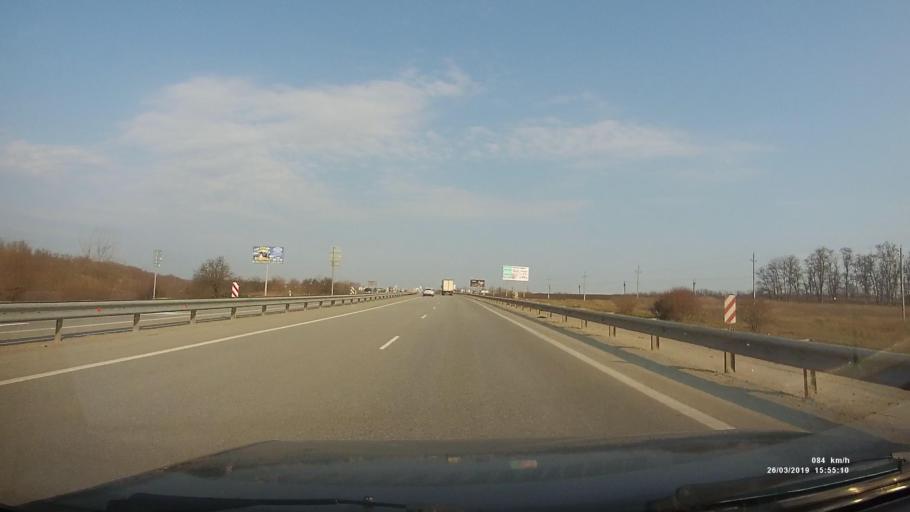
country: RU
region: Rostov
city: Kalinin
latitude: 47.2662
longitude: 39.5705
